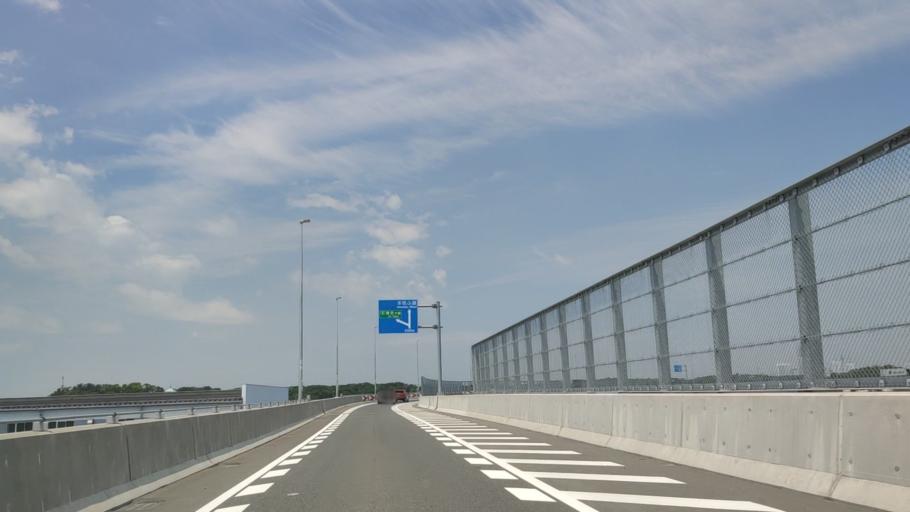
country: JP
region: Kanagawa
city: Yokohama
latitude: 35.4145
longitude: 139.6733
